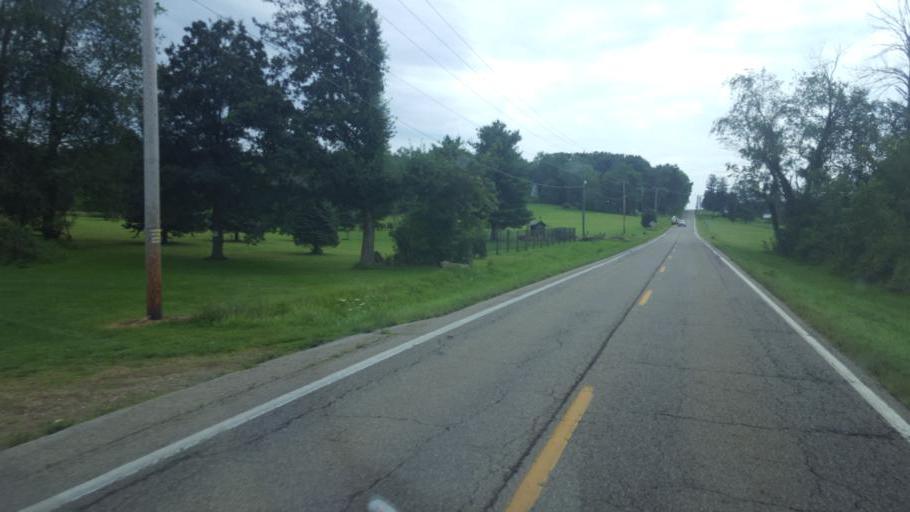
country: US
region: Ohio
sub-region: Knox County
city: Mount Vernon
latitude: 40.4116
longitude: -82.4561
